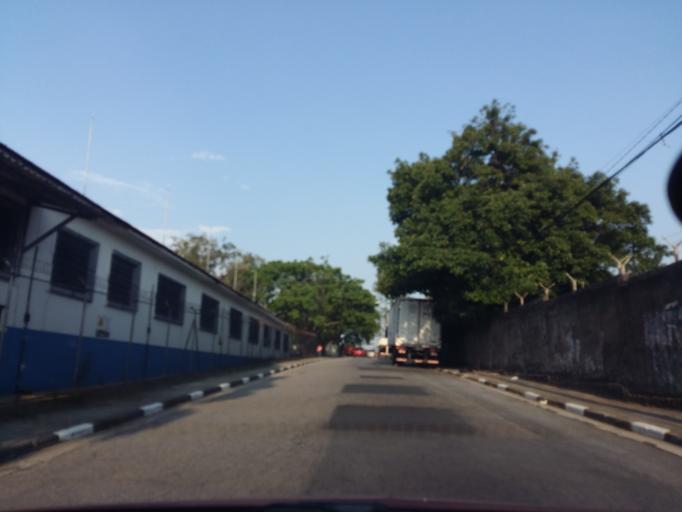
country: BR
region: Sao Paulo
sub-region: Diadema
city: Diadema
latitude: -23.6335
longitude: -46.6228
